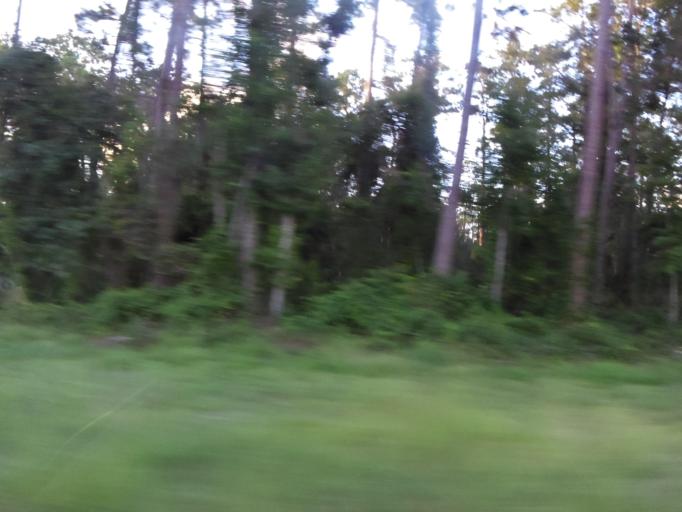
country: US
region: Georgia
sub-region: Glynn County
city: Brunswick
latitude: 31.1061
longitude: -81.6295
